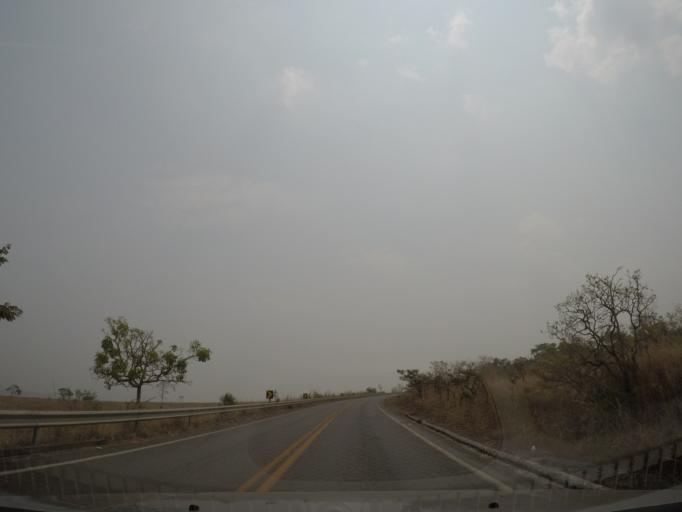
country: BR
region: Goias
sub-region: Pirenopolis
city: Pirenopolis
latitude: -15.9304
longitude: -48.8468
